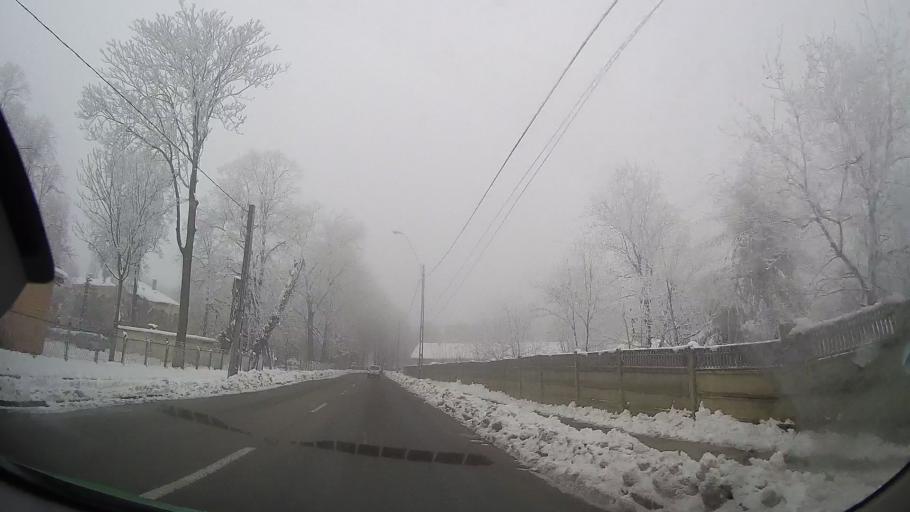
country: RO
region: Neamt
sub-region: Municipiul Roman
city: Roman
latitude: 46.9315
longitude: 26.9172
